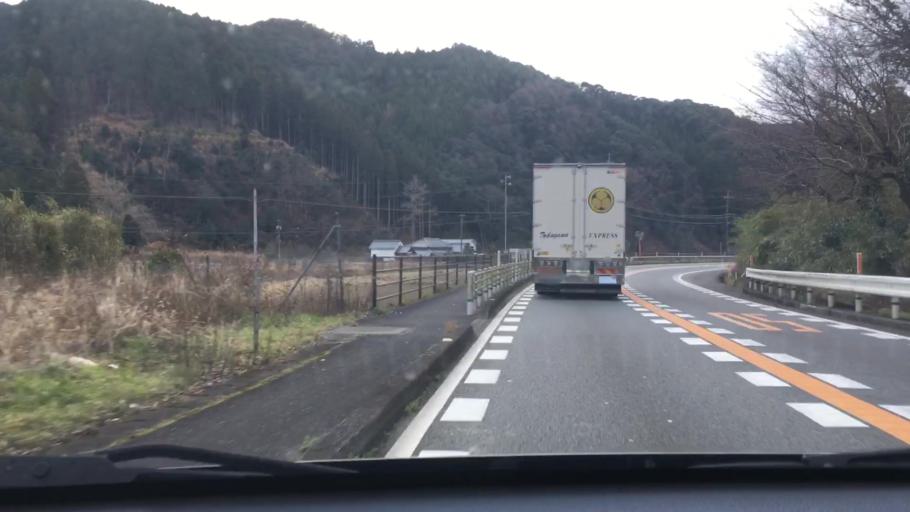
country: JP
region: Oita
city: Usuki
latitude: 33.0060
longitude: 131.7370
